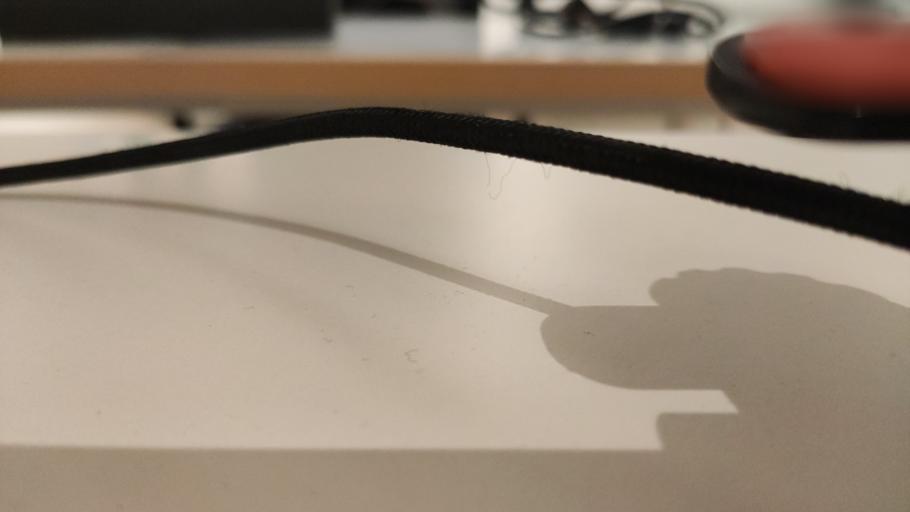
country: RU
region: Moskovskaya
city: Dorokhovo
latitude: 55.4349
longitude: 36.3518
